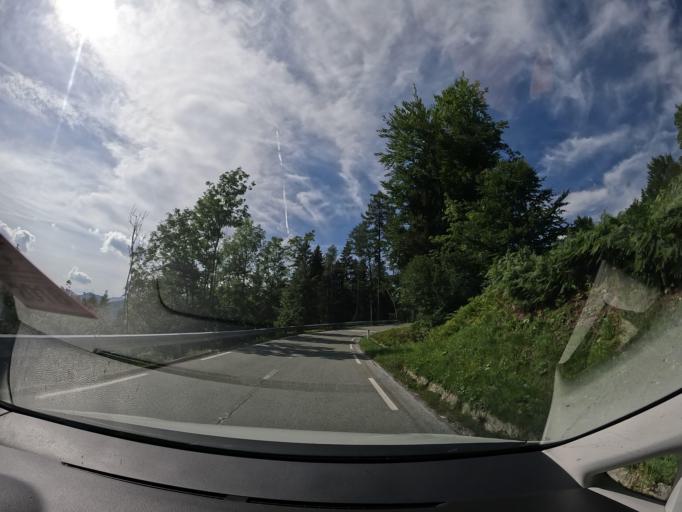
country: AT
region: Carinthia
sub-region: Politischer Bezirk Sankt Veit an der Glan
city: Liebenfels
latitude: 46.7198
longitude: 14.2511
